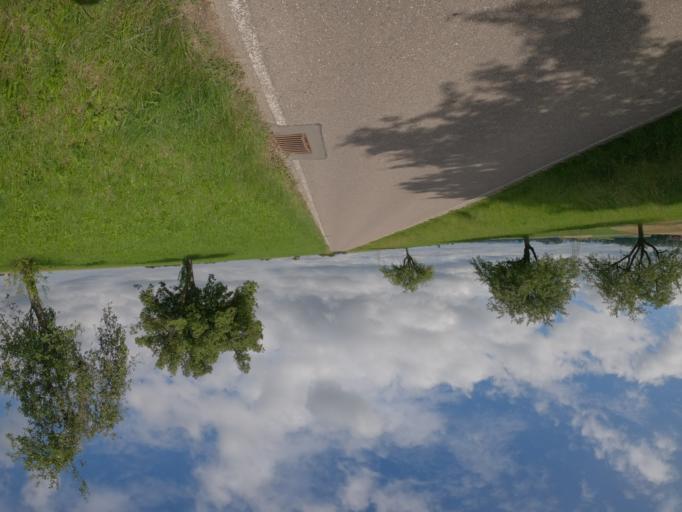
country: DE
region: Baden-Wuerttemberg
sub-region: Regierungsbezirk Stuttgart
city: Ebersbach an der Fils
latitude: 48.7034
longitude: 9.5196
